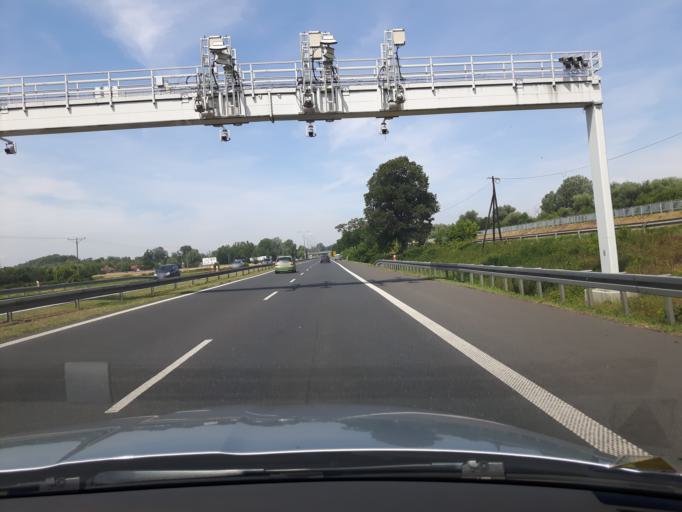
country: PL
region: Masovian Voivodeship
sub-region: Powiat nowodworski
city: Nowy Dwor Mazowiecki
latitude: 52.4060
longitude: 20.7042
